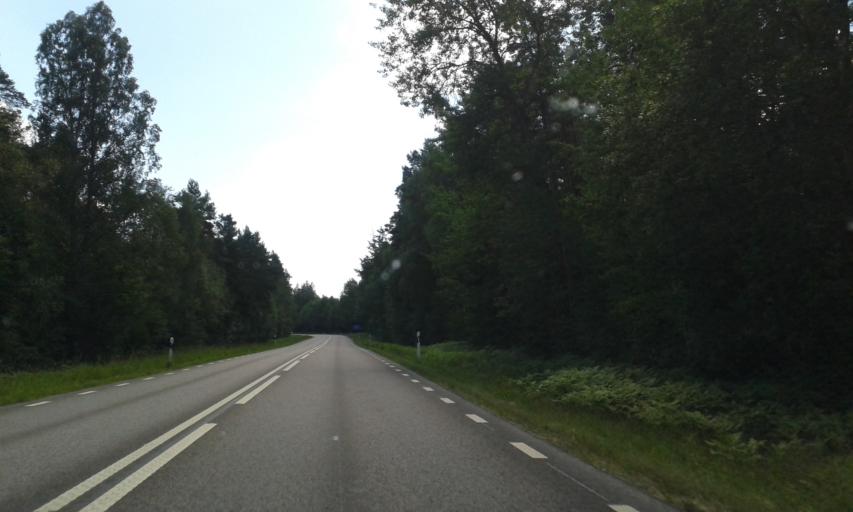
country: SE
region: Kronoberg
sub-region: Vaxjo Kommun
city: Ingelstad
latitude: 56.8177
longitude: 14.8809
